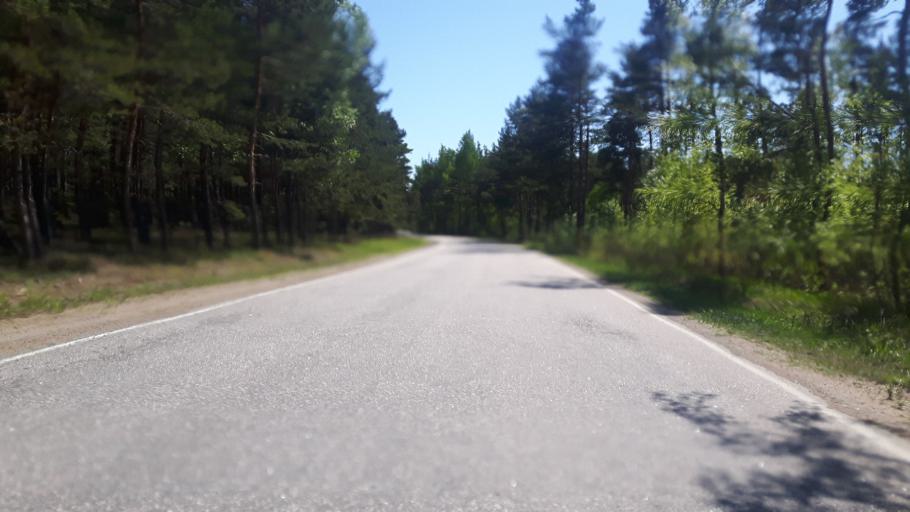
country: RU
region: Leningrad
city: Glebychevo
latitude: 60.3484
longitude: 28.8186
